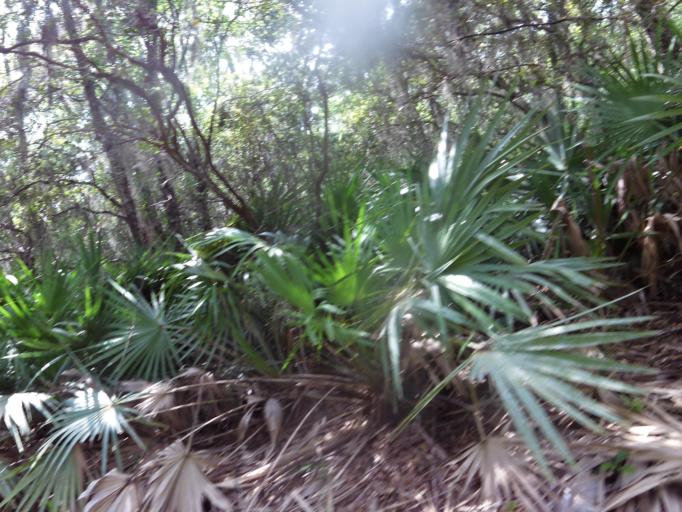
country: US
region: Florida
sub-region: Nassau County
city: Yulee
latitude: 30.4904
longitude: -81.5003
